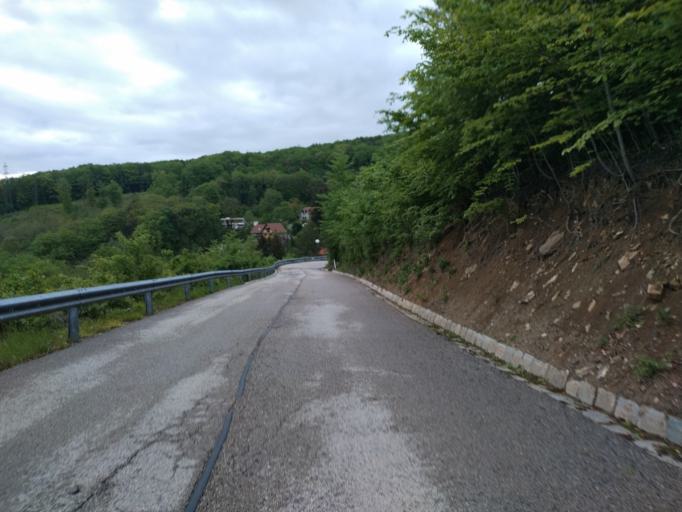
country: AT
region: Lower Austria
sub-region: Politischer Bezirk Wien-Umgebung
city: Mauerbach
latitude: 48.2442
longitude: 16.2182
